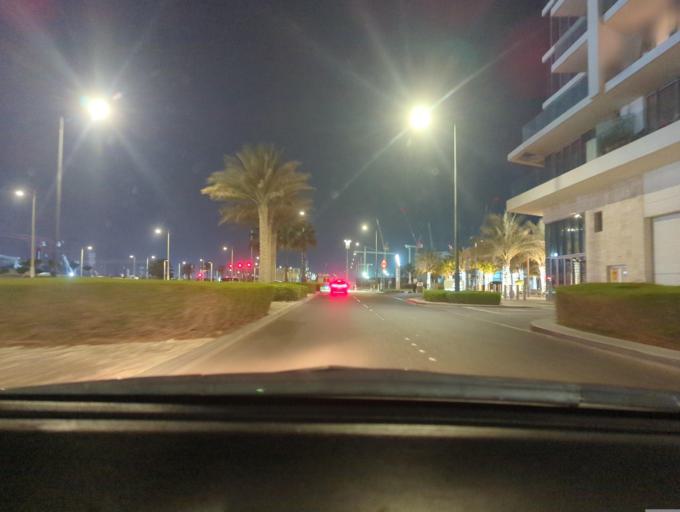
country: AE
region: Abu Dhabi
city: Abu Dhabi
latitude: 24.5382
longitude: 54.4076
